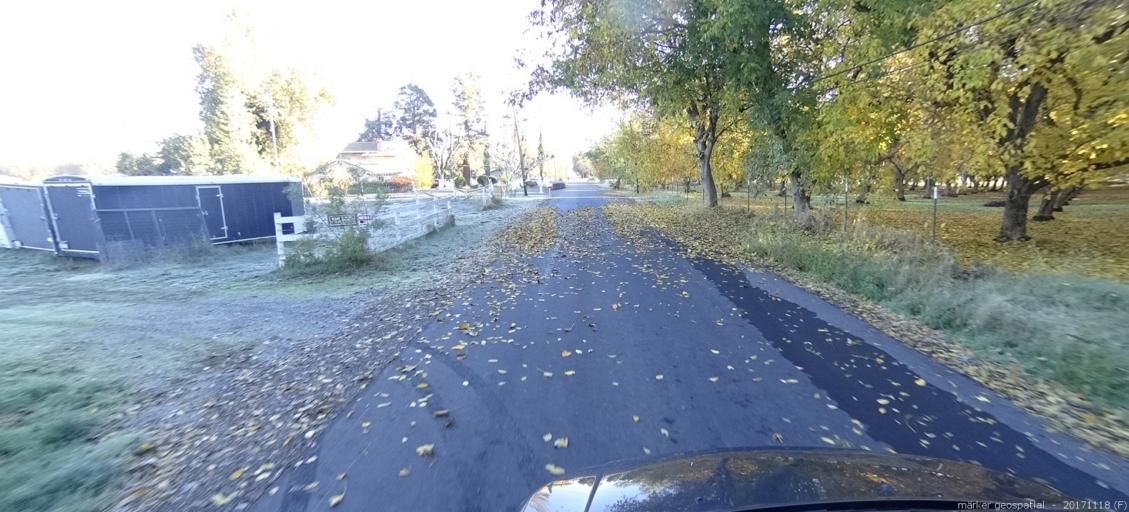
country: US
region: California
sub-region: Shasta County
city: Anderson
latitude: 40.4507
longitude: -122.2612
